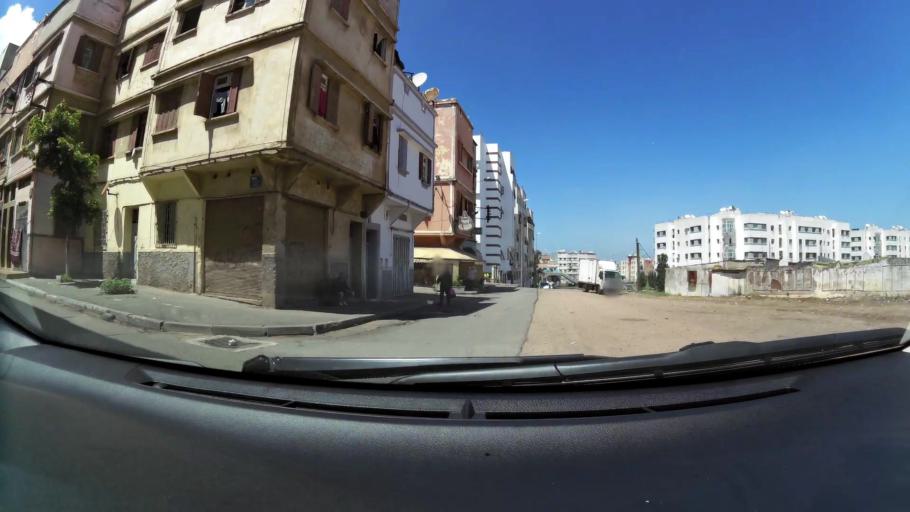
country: MA
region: Grand Casablanca
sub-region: Casablanca
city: Casablanca
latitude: 33.5604
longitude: -7.5842
